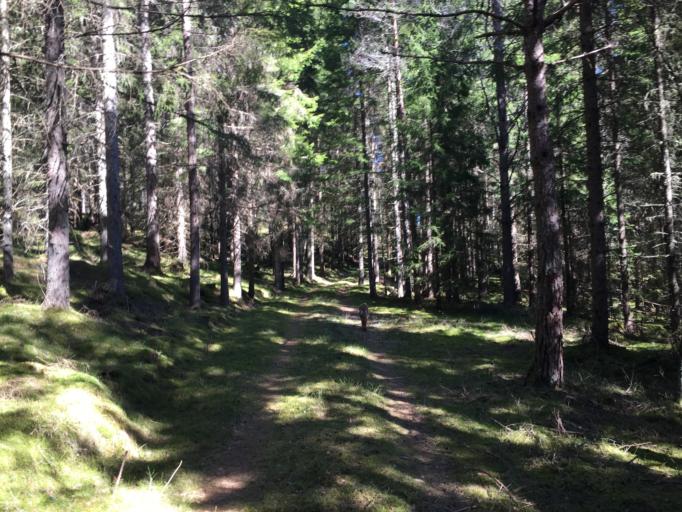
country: SE
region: Joenkoeping
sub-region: Vaggeryds Kommun
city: Skillingaryd
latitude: 57.4649
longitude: 14.0038
